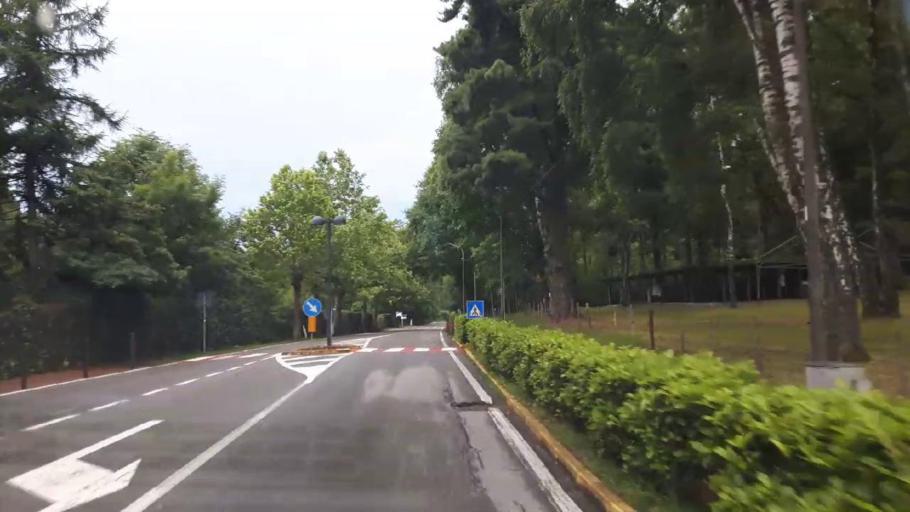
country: IT
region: Piedmont
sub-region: Provincia Verbano-Cusio-Ossola
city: Gignese
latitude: 45.8694
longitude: 8.5135
